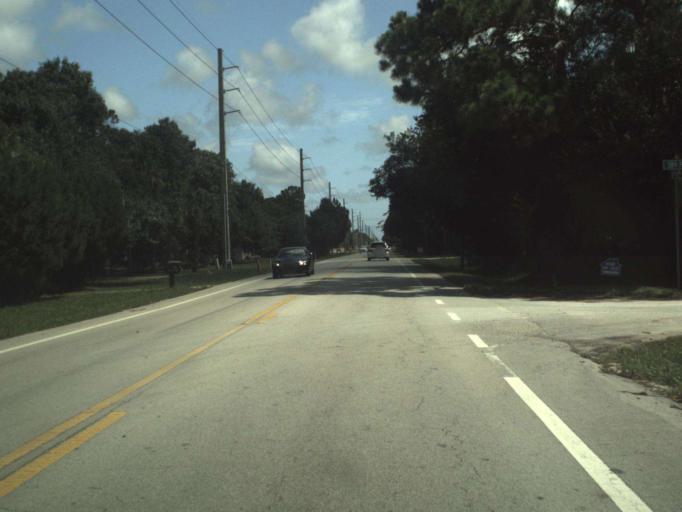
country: US
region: Florida
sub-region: Indian River County
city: Gifford
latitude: 27.6619
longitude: -80.4464
